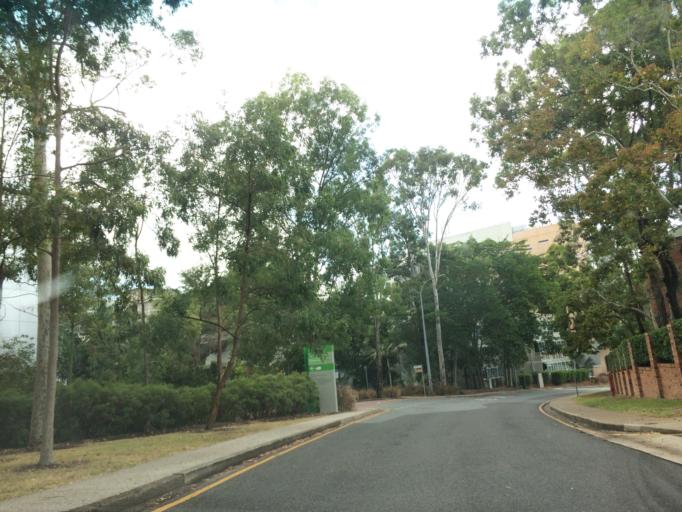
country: AU
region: Queensland
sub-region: Brisbane
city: Yeronga
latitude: -27.5012
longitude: 153.0130
